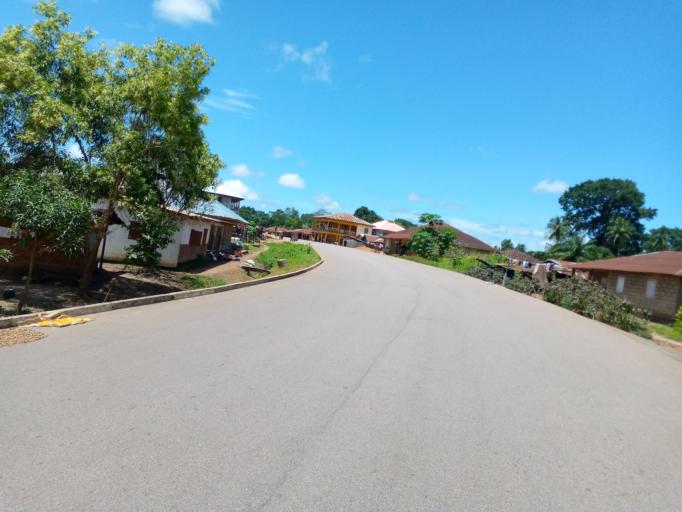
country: SL
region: Northern Province
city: Makeni
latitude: 9.0327
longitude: -12.1591
